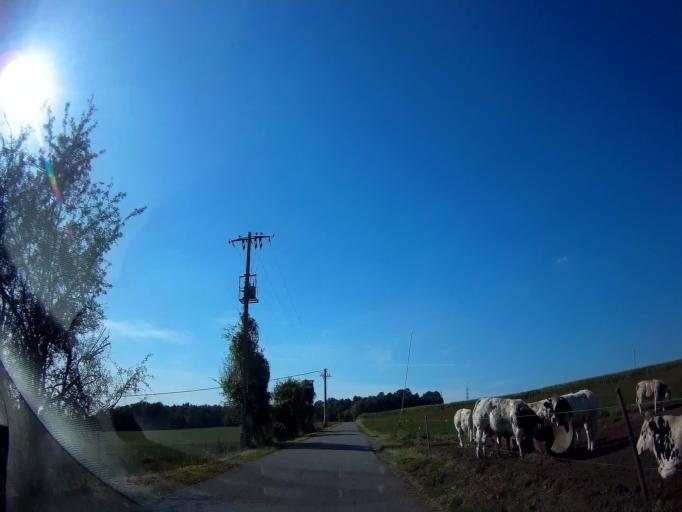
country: BE
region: Wallonia
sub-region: Province de Namur
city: Dinant
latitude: 50.2487
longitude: 4.9442
